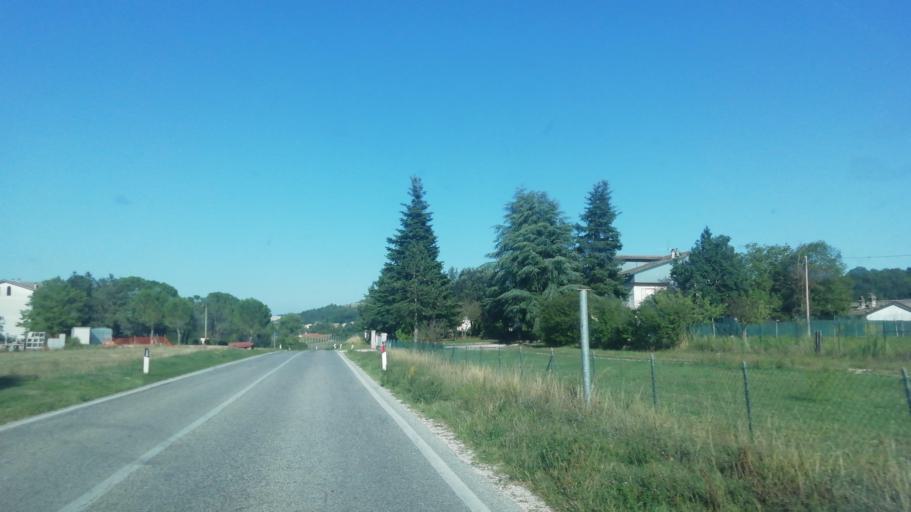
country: IT
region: The Marches
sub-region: Provincia di Pesaro e Urbino
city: Pergola
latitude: 43.5557
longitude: 12.8169
